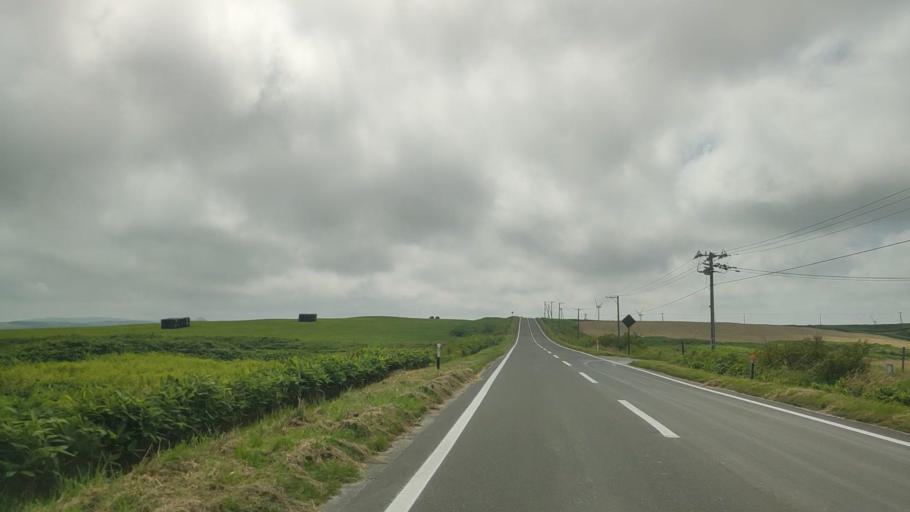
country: JP
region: Hokkaido
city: Makubetsu
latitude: 45.4904
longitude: 141.9370
